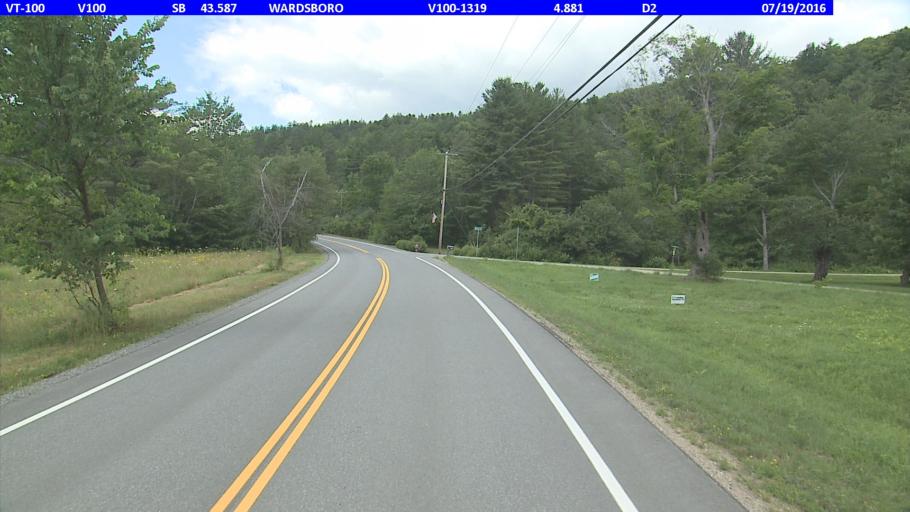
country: US
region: Vermont
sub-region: Windham County
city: Dover
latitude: 43.0686
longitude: -72.8625
